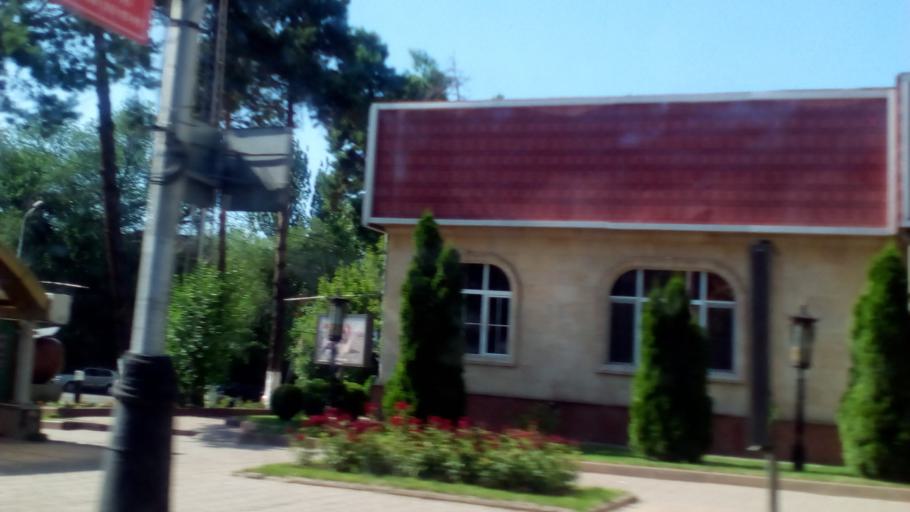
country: KZ
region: Almaty Qalasy
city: Almaty
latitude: 43.2498
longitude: 76.9430
